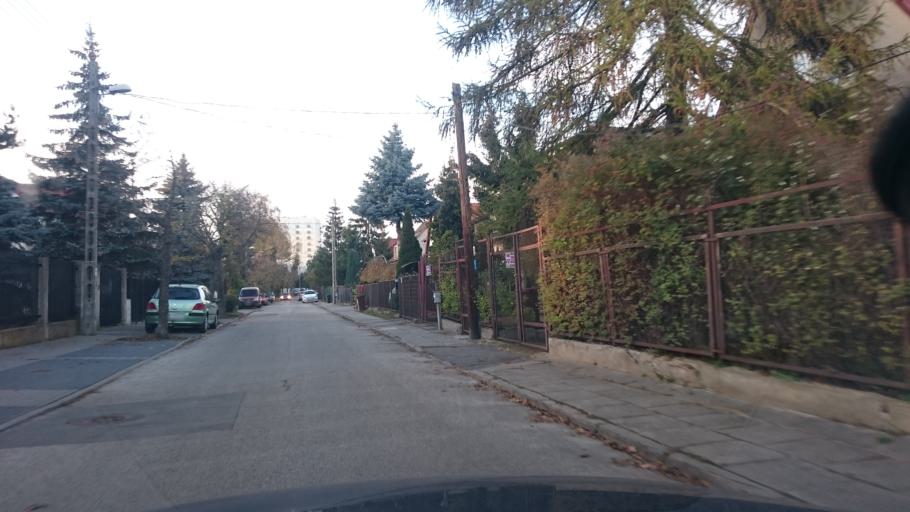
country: PL
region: Pomeranian Voivodeship
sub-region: Sopot
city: Sopot
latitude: 54.3996
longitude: 18.5814
